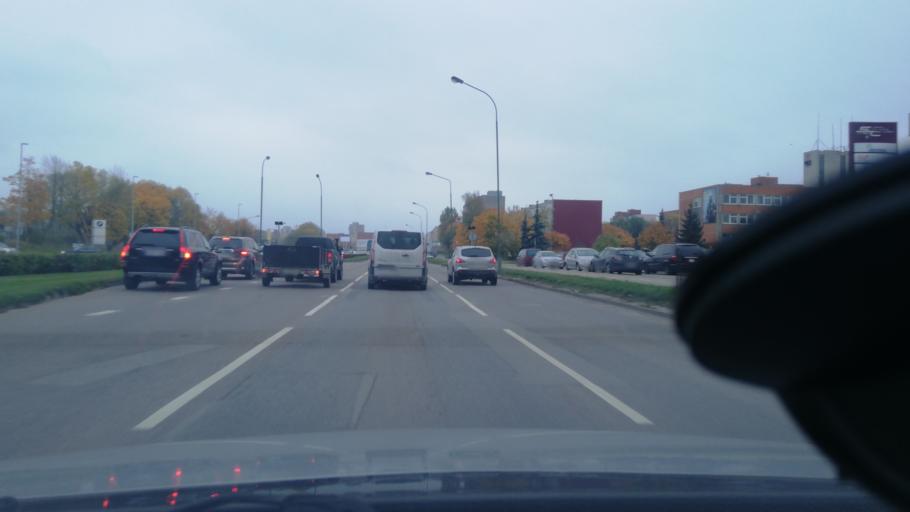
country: LT
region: Klaipedos apskritis
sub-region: Klaipeda
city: Klaipeda
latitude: 55.6816
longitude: 21.1861
